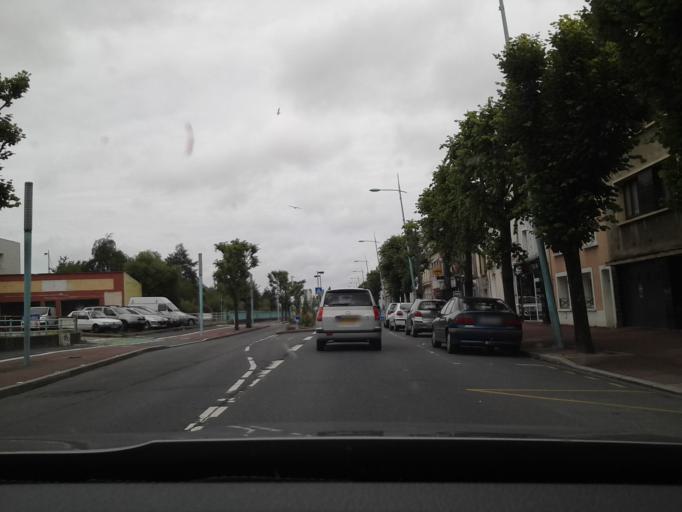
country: FR
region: Lower Normandy
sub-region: Departement de la Manche
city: Cherbourg-Octeville
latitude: 49.6289
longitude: -1.6181
